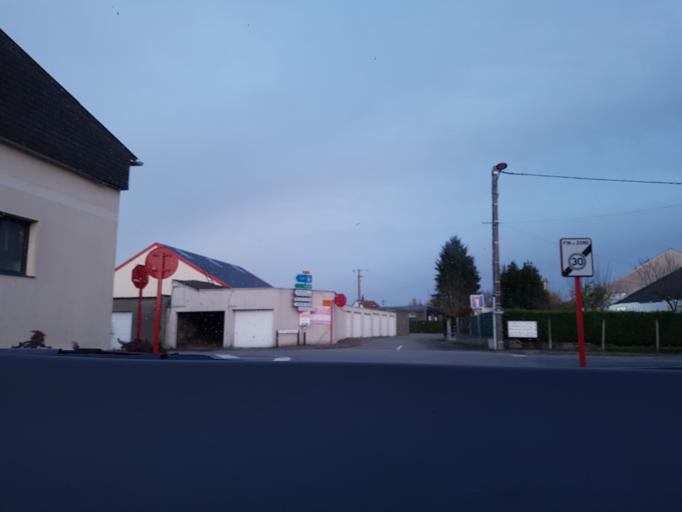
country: FR
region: Pays de la Loire
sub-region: Departement de la Mayenne
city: Cosse-le-Vivien
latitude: 47.9442
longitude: -0.9112
